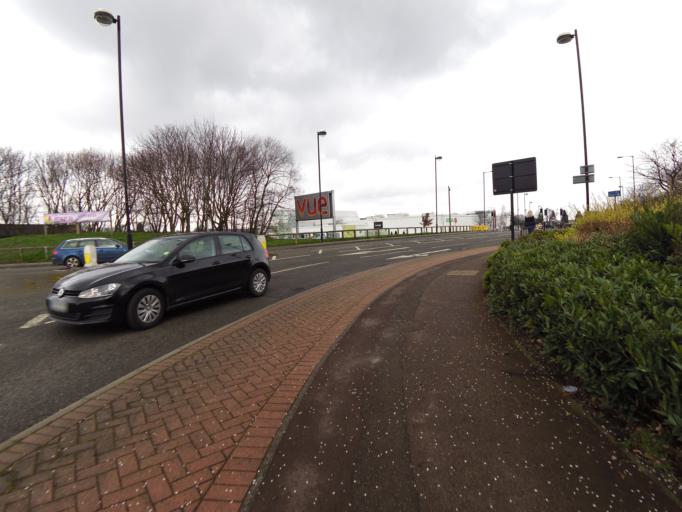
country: GB
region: England
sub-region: Doncaster
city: Doncaster
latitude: 53.5148
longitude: -1.1010
